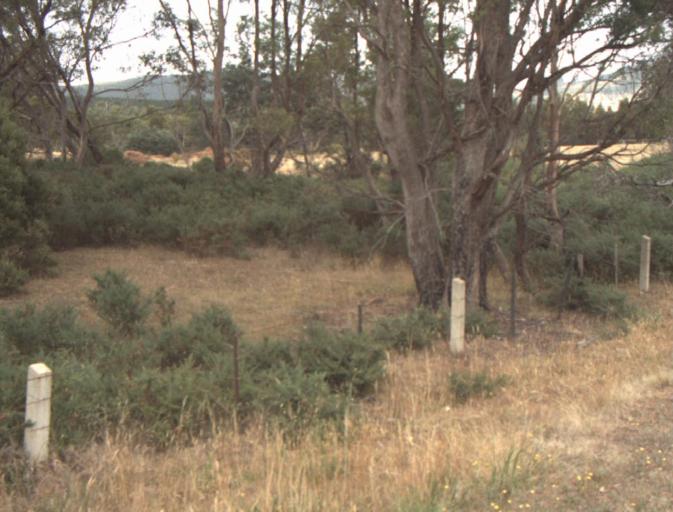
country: AU
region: Tasmania
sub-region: Northern Midlands
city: Evandale
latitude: -41.4813
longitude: 147.5069
